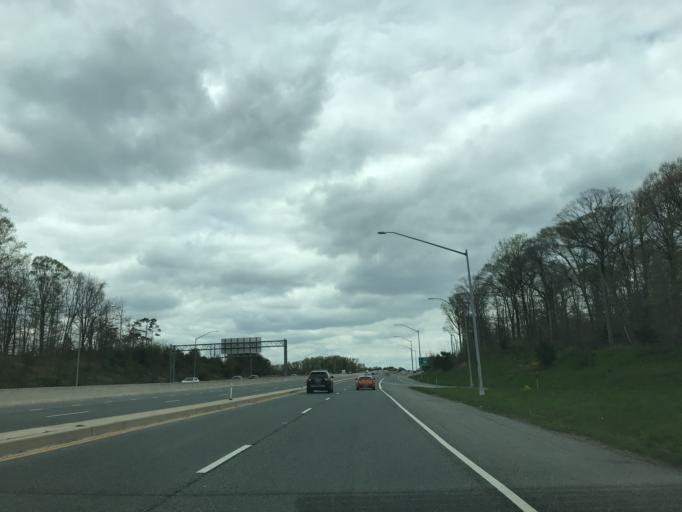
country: US
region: Maryland
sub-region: Harford County
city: Joppatowne
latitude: 39.4596
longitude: -76.3114
